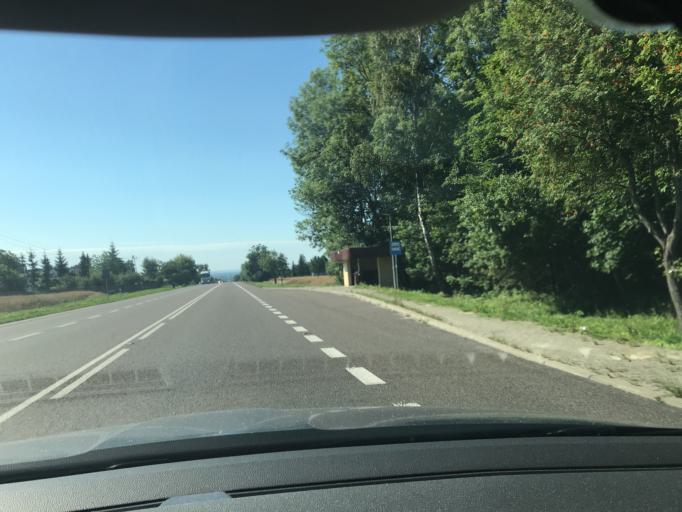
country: PL
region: Lublin Voivodeship
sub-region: Powiat zamojski
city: Stary Zamosc
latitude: 50.8468
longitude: 23.1674
